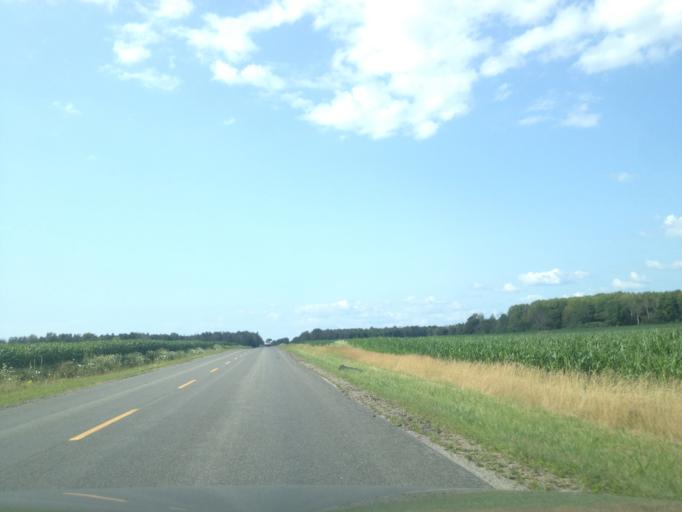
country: CA
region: Ontario
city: Aylmer
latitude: 42.6769
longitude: -80.8599
